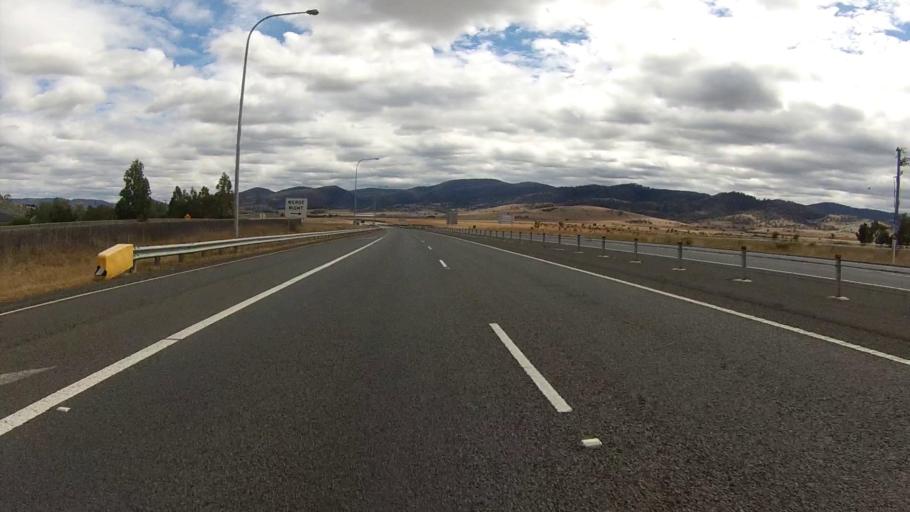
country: AU
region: Tasmania
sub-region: Brighton
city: Bridgewater
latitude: -42.6915
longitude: 147.2783
